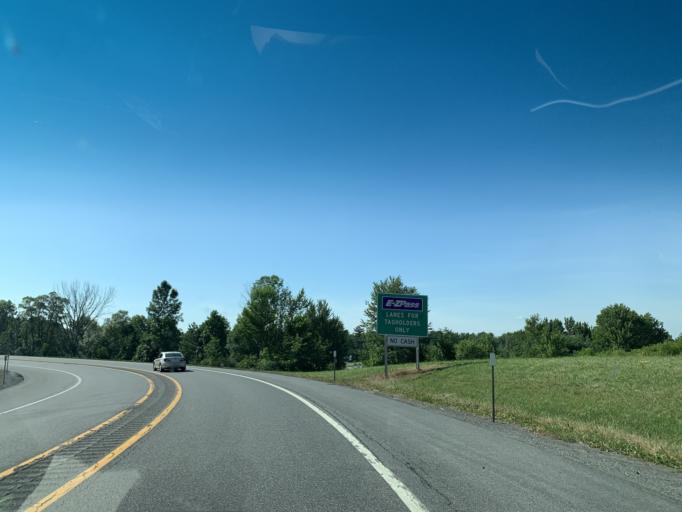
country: US
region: New York
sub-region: Oneida County
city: Sherrill
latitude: 43.1256
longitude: -75.5803
